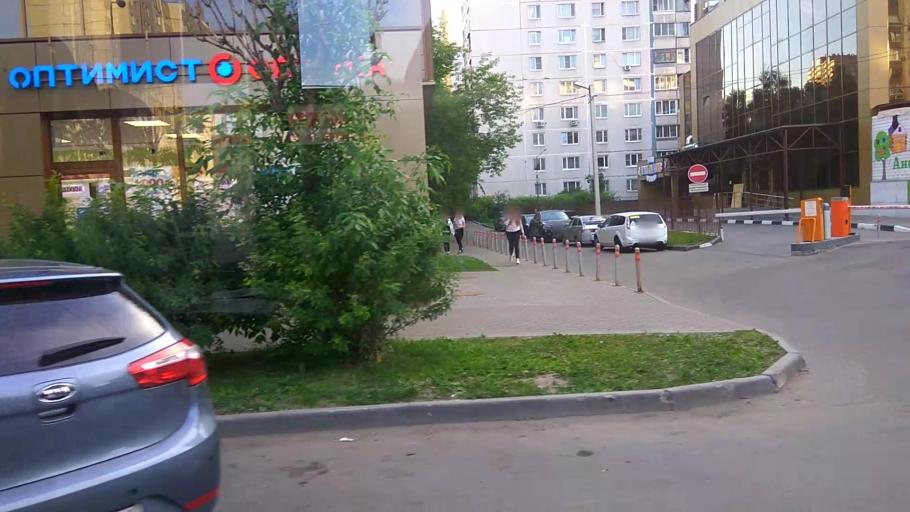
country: RU
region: Moskovskaya
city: Yubileyny
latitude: 55.9200
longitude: 37.8682
